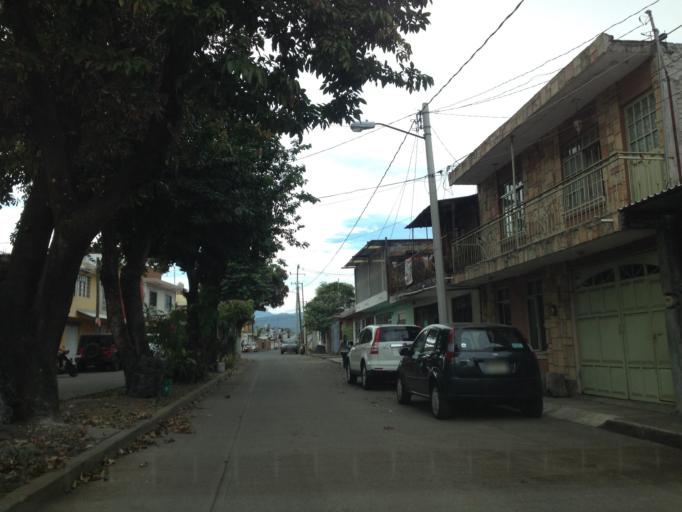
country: MX
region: Michoacan
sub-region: Uruapan
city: Uruapan
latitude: 19.4089
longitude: -102.0379
